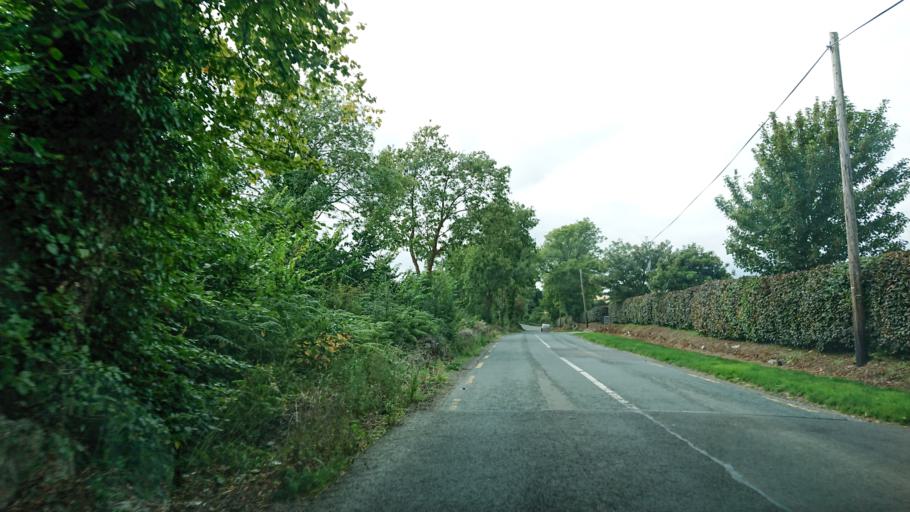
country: IE
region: Munster
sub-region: County Cork
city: Mallow
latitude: 52.1520
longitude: -8.5317
